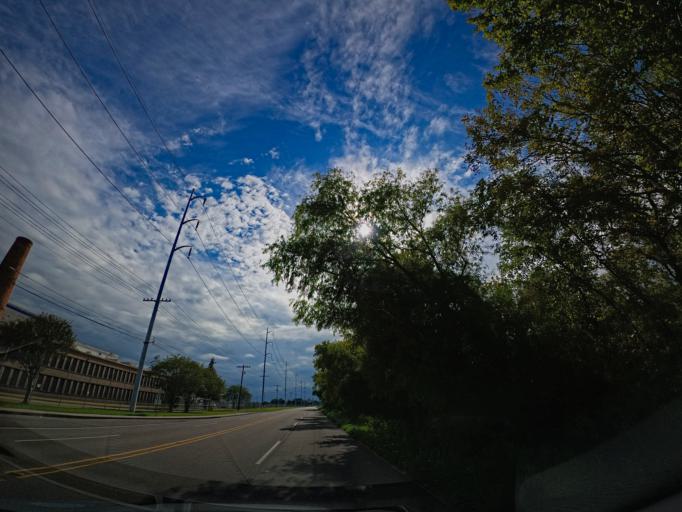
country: US
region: Louisiana
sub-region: Saint Bernard Parish
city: Chalmette
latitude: 30.0269
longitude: -89.9173
